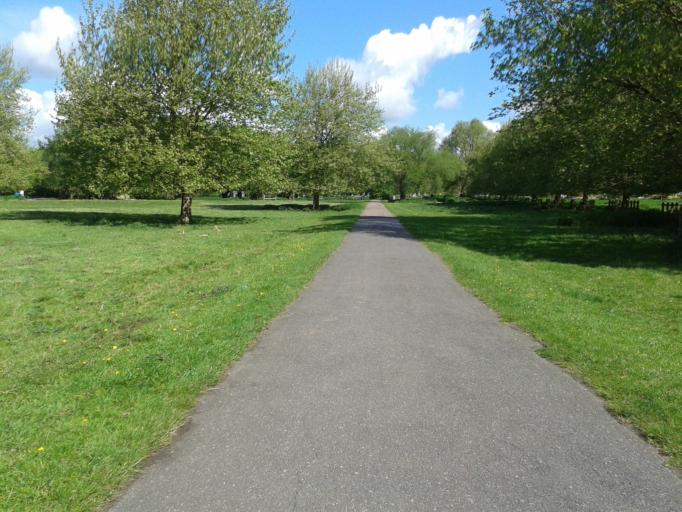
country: GB
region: England
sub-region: Cambridgeshire
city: Cambridge
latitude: 52.2154
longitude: 0.1465
